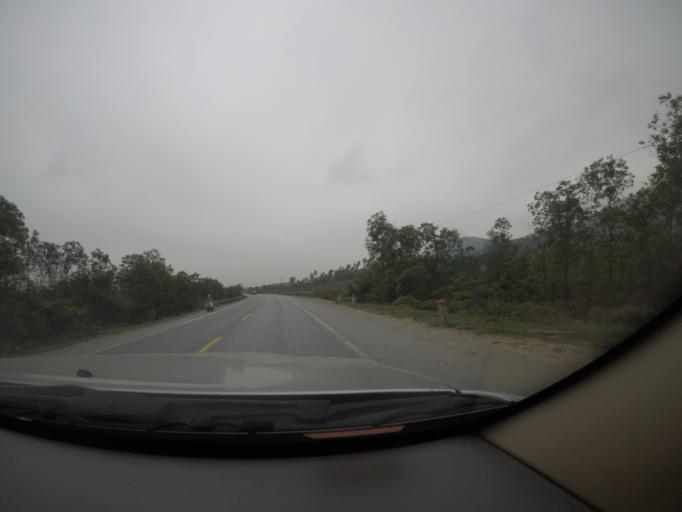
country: VN
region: Ha Tinh
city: Ky Anh
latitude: 18.0281
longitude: 106.3307
